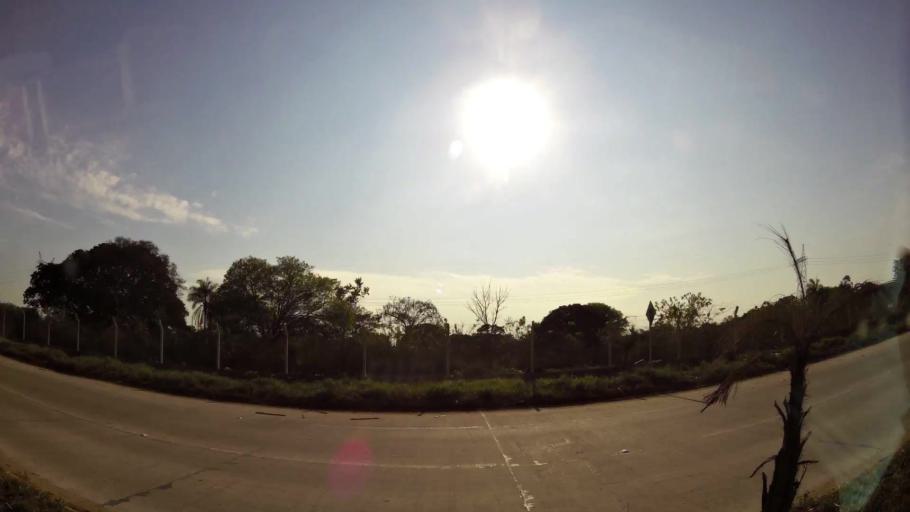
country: BO
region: Santa Cruz
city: Santa Cruz de la Sierra
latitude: -17.7065
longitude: -63.1280
